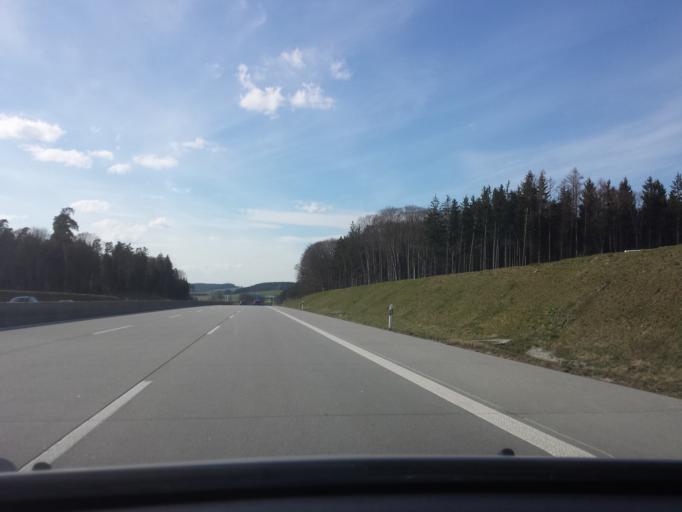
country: DE
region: Bavaria
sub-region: Swabia
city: Adelzhausen
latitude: 48.3428
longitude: 11.1506
